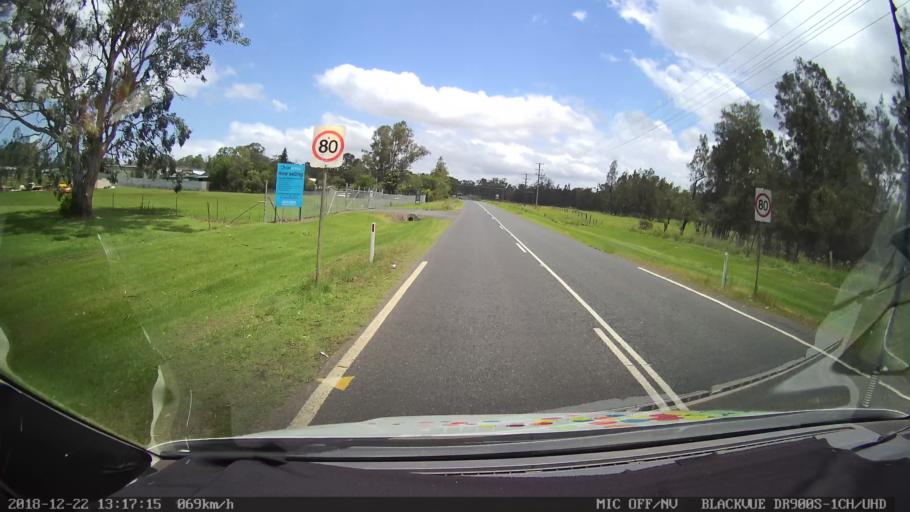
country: AU
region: New South Wales
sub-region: Clarence Valley
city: South Grafton
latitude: -29.7343
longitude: 152.9393
